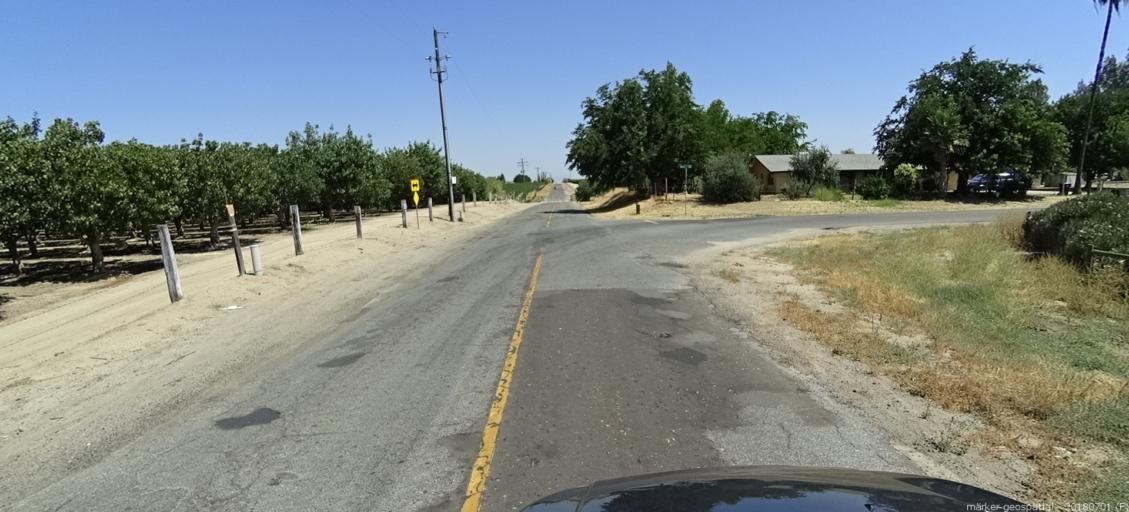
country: US
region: California
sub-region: Madera County
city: Madera Acres
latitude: 37.0664
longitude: -120.0293
